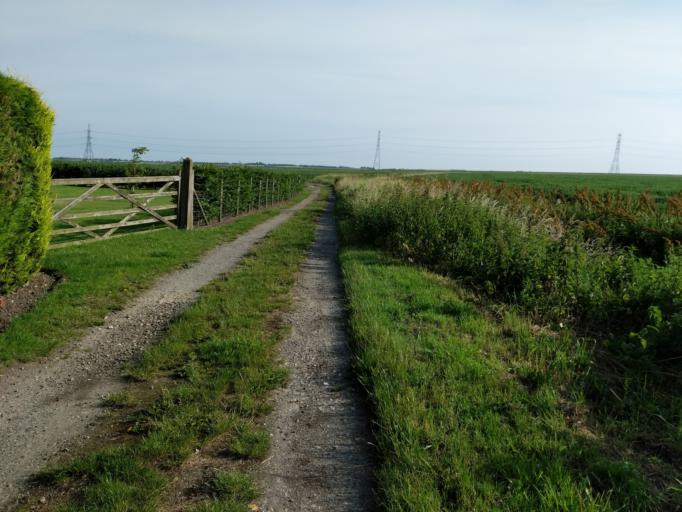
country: GB
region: England
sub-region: Kent
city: Faversham
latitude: 51.3321
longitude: 0.9147
